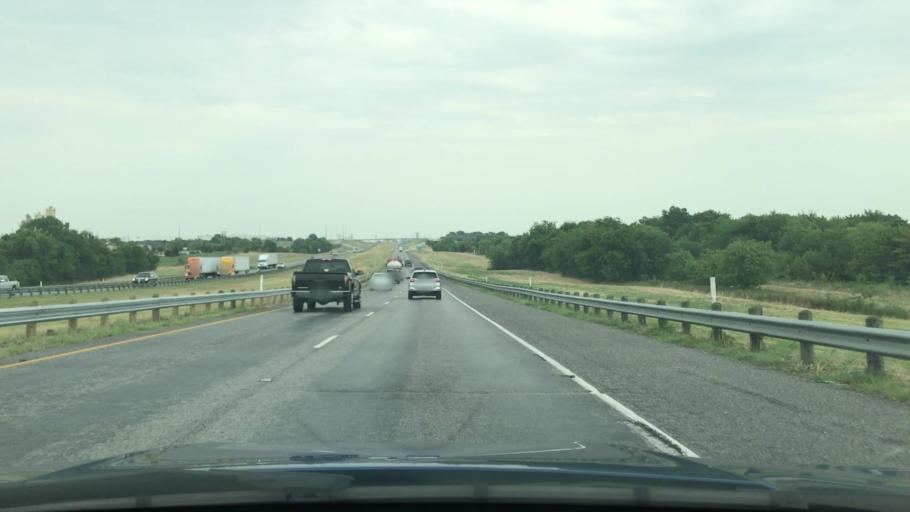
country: US
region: Texas
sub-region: Kaufman County
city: Talty
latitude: 32.7364
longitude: -96.3532
